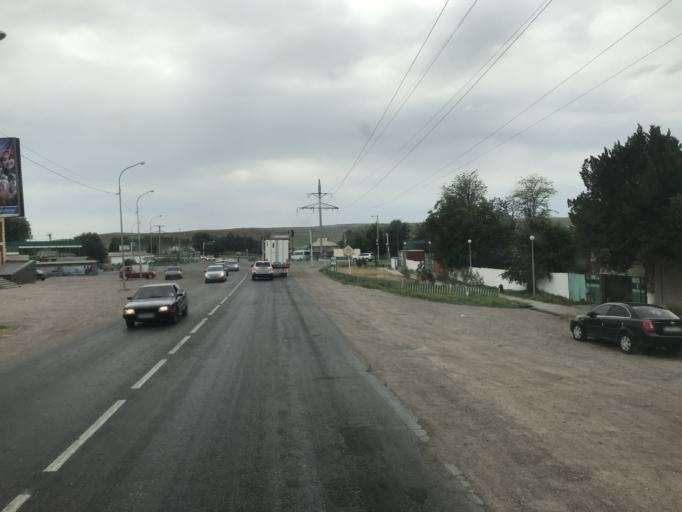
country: KZ
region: Ongtustik Qazaqstan
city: Saryaghash
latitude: 41.4900
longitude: 69.2626
